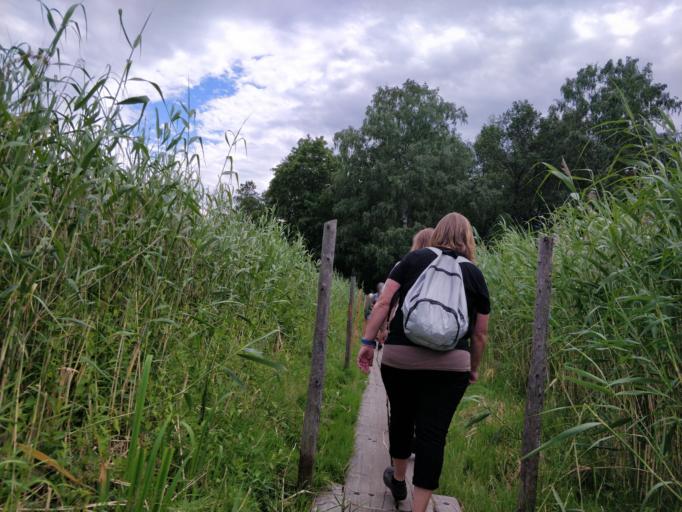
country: FI
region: Uusimaa
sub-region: Helsinki
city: Helsinki
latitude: 60.2052
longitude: 24.9955
